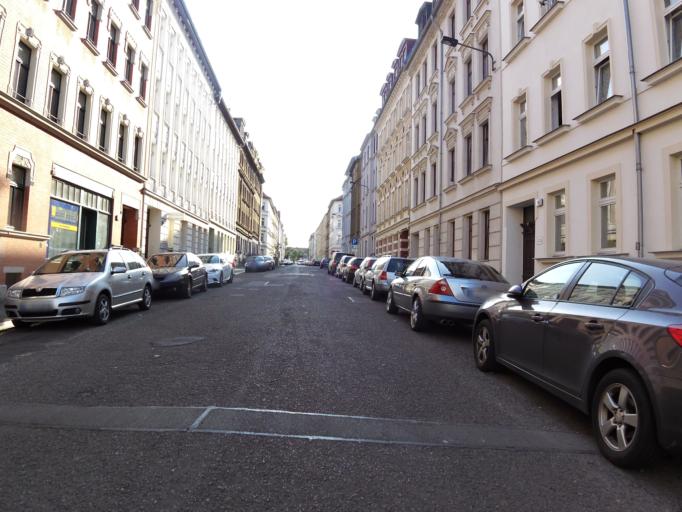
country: DE
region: Saxony
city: Leipzig
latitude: 51.3402
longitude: 12.3273
